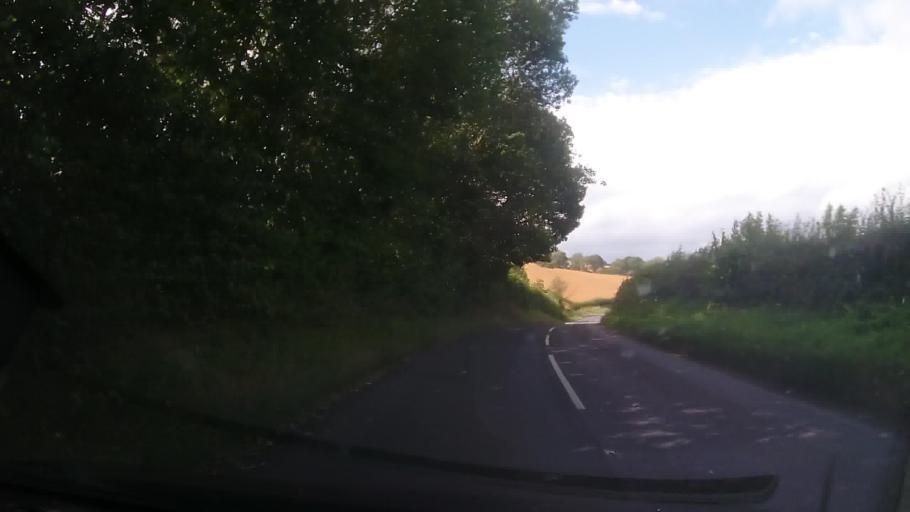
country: GB
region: England
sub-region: Shropshire
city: Acton
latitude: 52.4578
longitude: -3.0153
